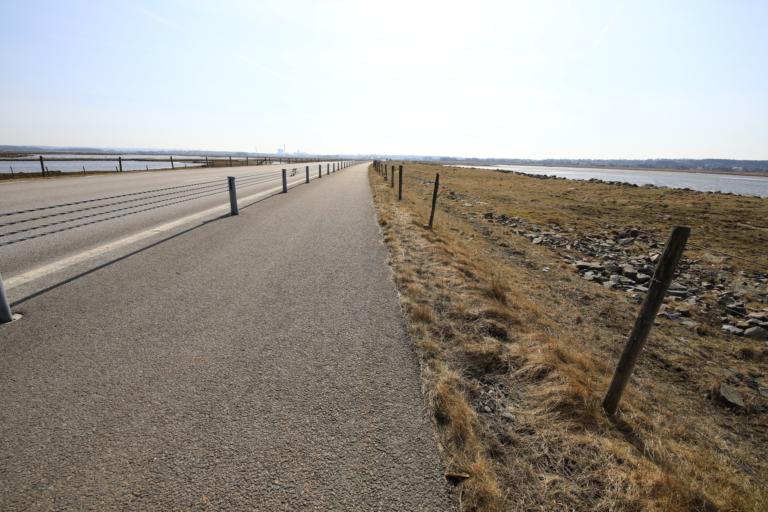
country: SE
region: Halland
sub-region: Kungsbacka Kommun
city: Frillesas
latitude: 57.2499
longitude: 12.1291
